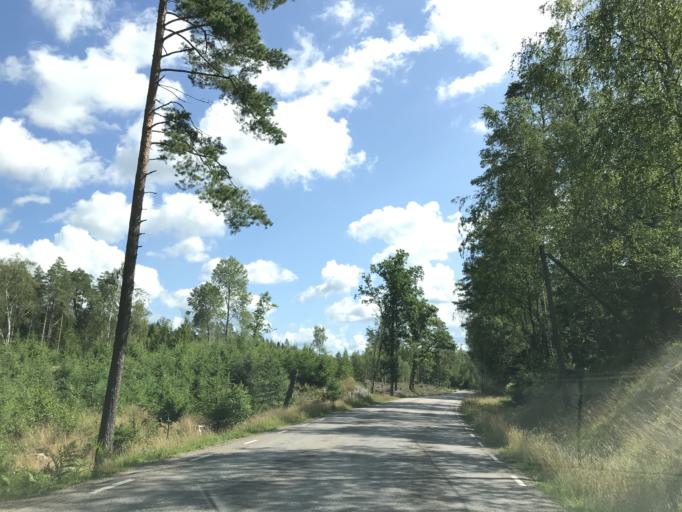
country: SE
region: Halland
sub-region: Laholms Kommun
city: Knared
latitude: 56.5214
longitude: 13.3711
